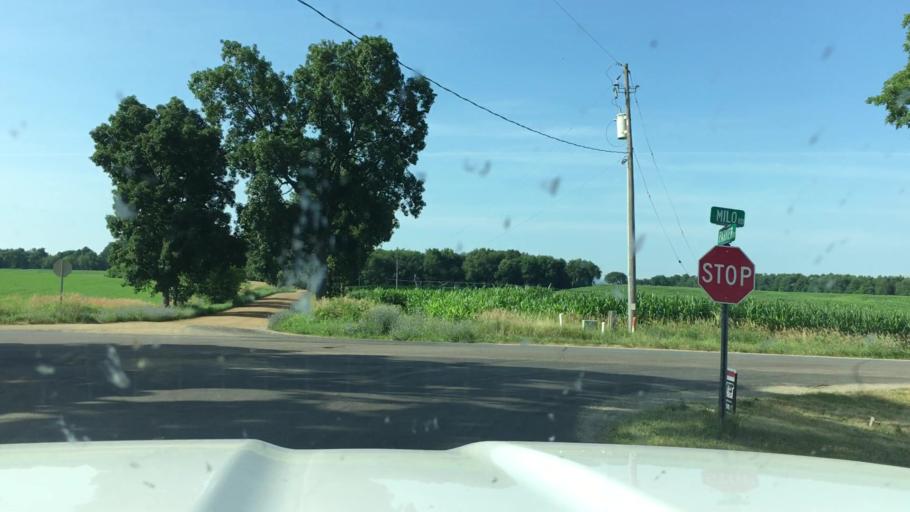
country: US
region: Michigan
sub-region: Barry County
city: Stony Point
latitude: 42.4571
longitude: -85.4447
